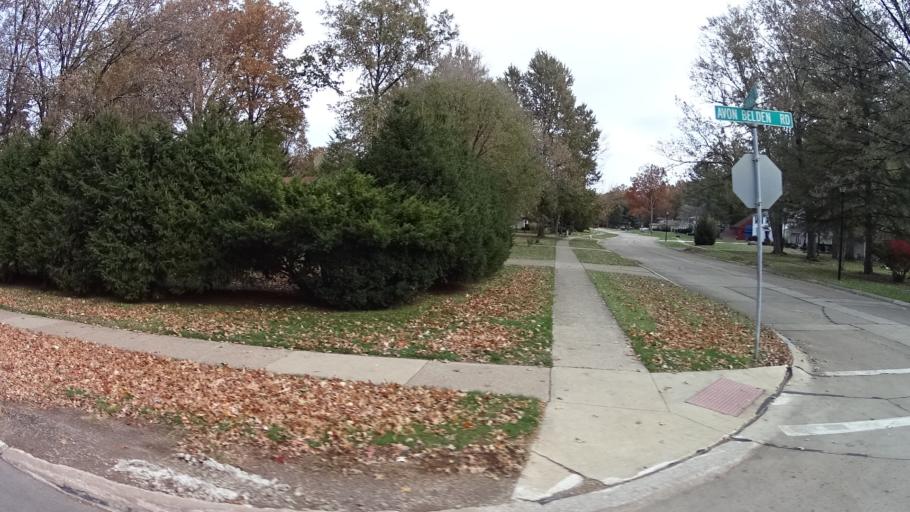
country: US
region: Ohio
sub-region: Lorain County
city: Avon Lake
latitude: 41.5051
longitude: -82.0187
